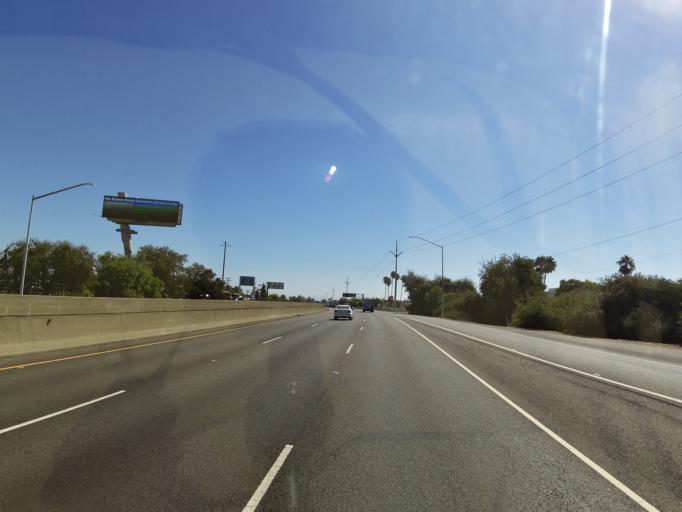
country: US
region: California
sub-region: Sacramento County
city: Arden-Arcade
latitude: 38.6313
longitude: -121.3993
